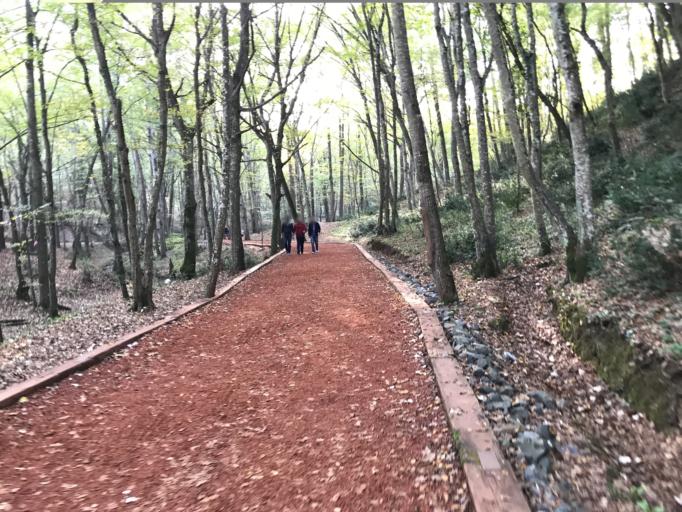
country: TR
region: Istanbul
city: Kemerburgaz
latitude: 41.1737
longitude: 28.9564
